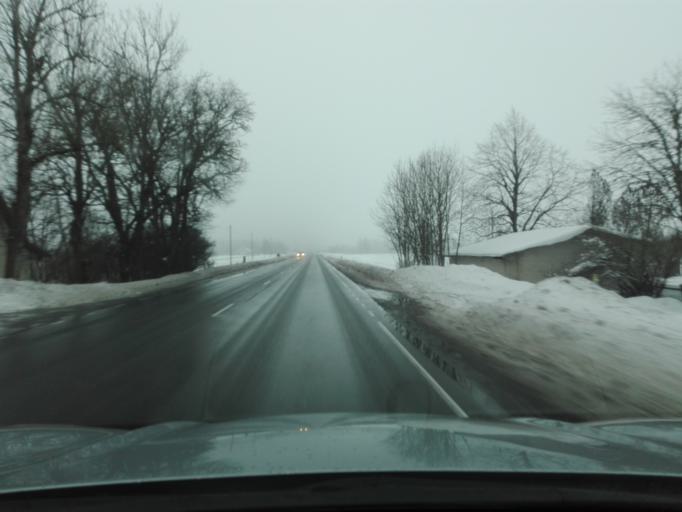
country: EE
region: Raplamaa
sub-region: Kohila vald
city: Kohila
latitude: 59.2026
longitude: 24.7822
